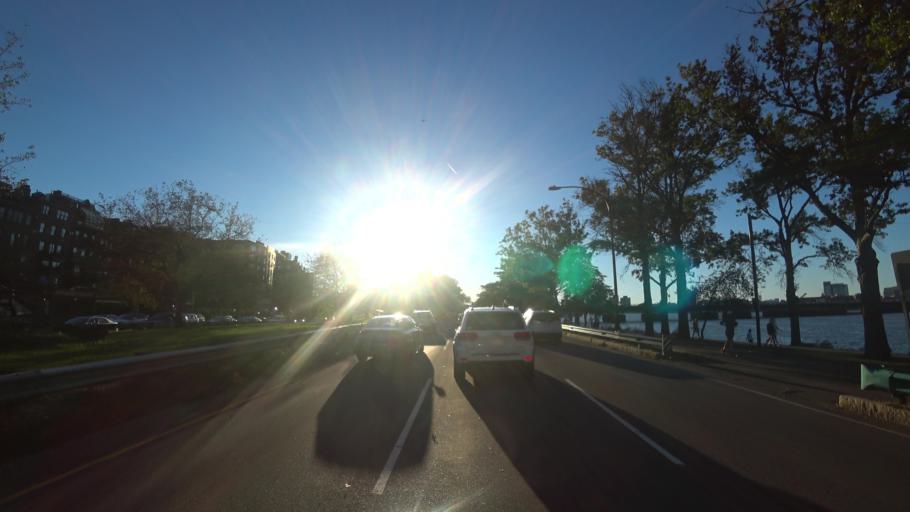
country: US
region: Massachusetts
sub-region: Middlesex County
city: Cambridge
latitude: 42.3522
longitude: -71.0880
